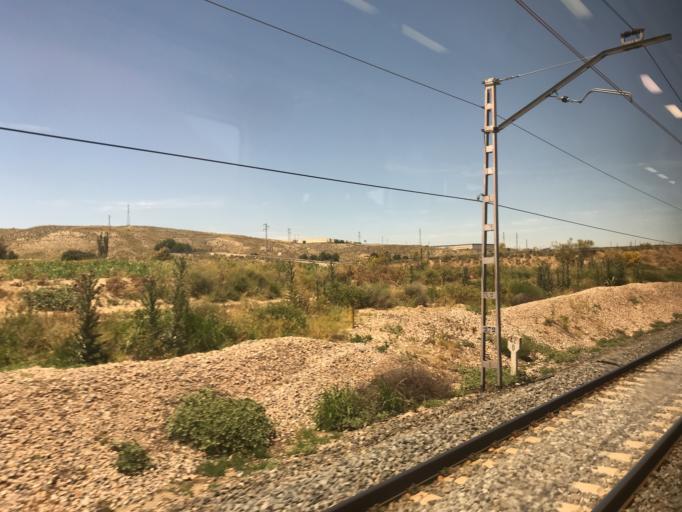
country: ES
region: Madrid
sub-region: Provincia de Madrid
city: Aranjuez
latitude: 40.0861
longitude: -3.6325
